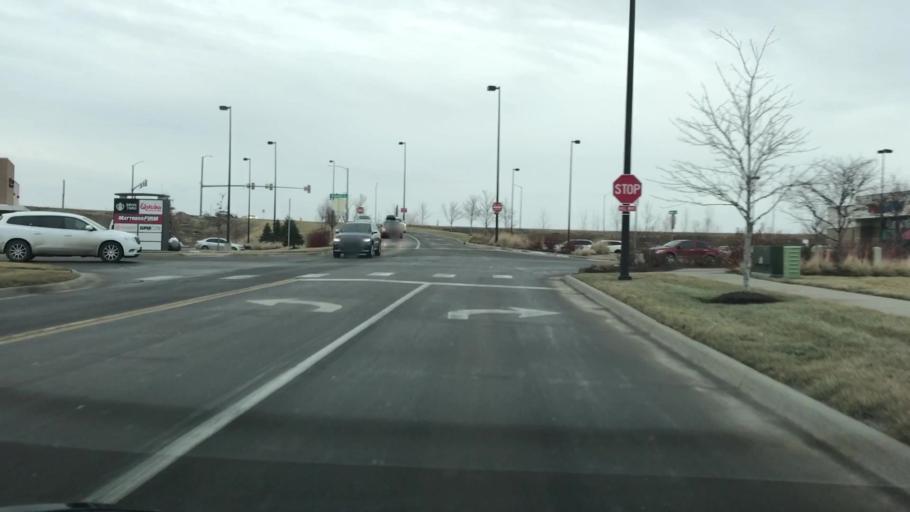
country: US
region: Iowa
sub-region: Pottawattamie County
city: Council Bluffs
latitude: 41.2208
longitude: -95.8354
